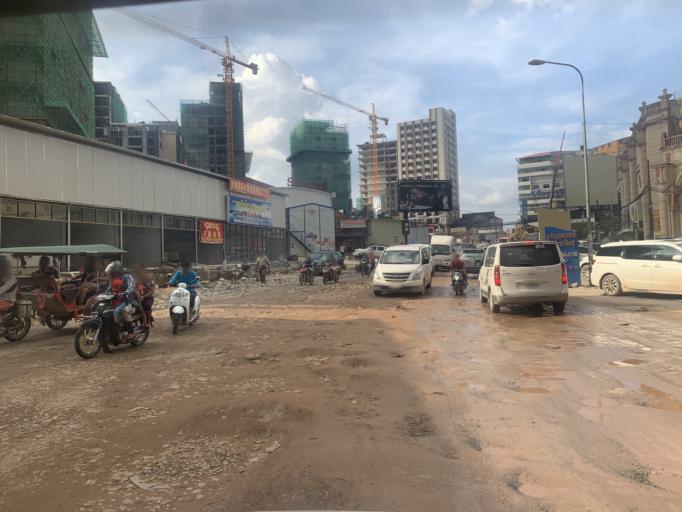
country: KH
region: Preah Sihanouk
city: Sihanoukville
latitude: 10.6090
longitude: 103.5239
